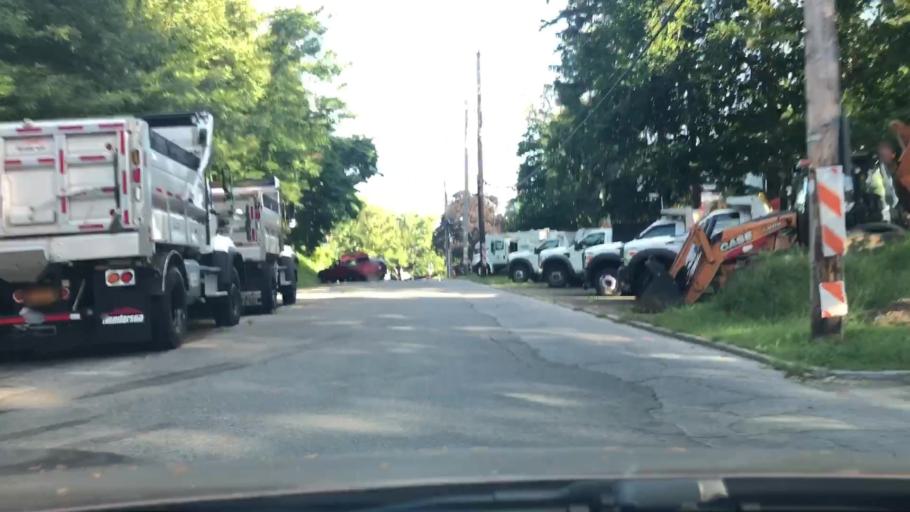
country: US
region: New York
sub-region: Westchester County
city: Bronxville
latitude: 40.9346
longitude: -73.8312
